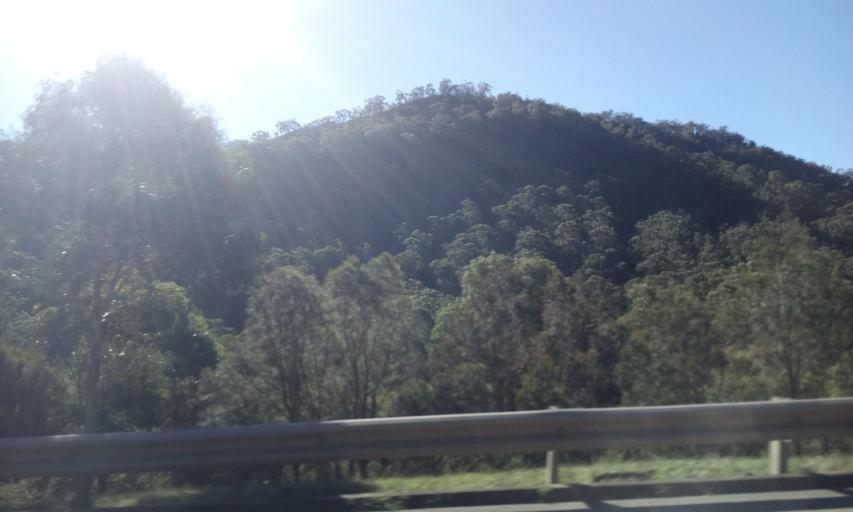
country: AU
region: New South Wales
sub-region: Wingecarribee
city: Mittagong
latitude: -34.4322
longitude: 150.4488
